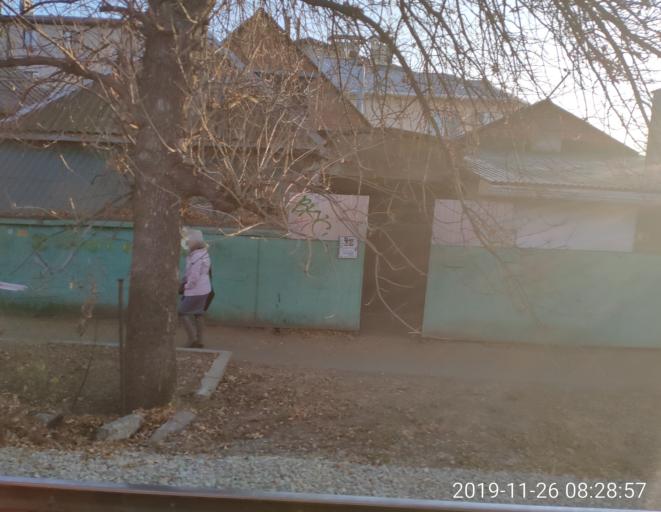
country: RU
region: Krasnodarskiy
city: Krasnodar
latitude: 45.0533
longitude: 39.0028
